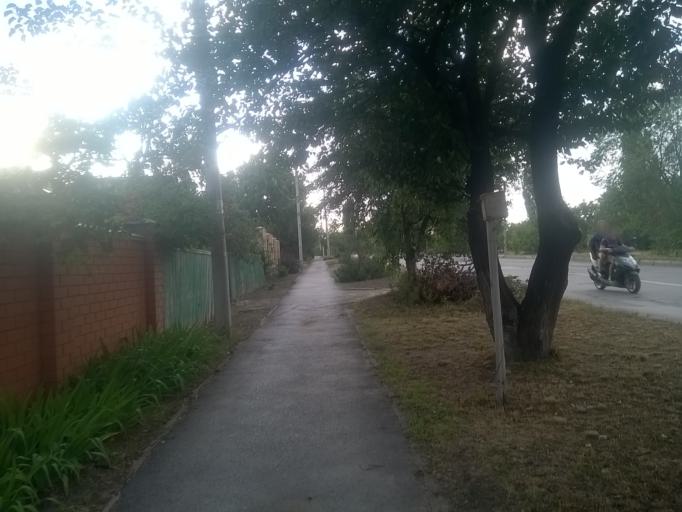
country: RU
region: Rostov
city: Donetsk
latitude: 48.3349
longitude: 39.9581
